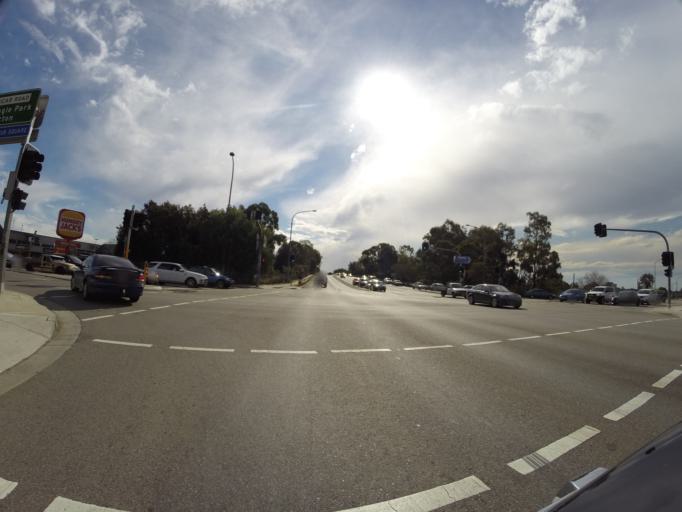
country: AU
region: New South Wales
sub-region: Campbelltown Municipality
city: Campbelltown
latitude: -34.0722
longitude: 150.8057
